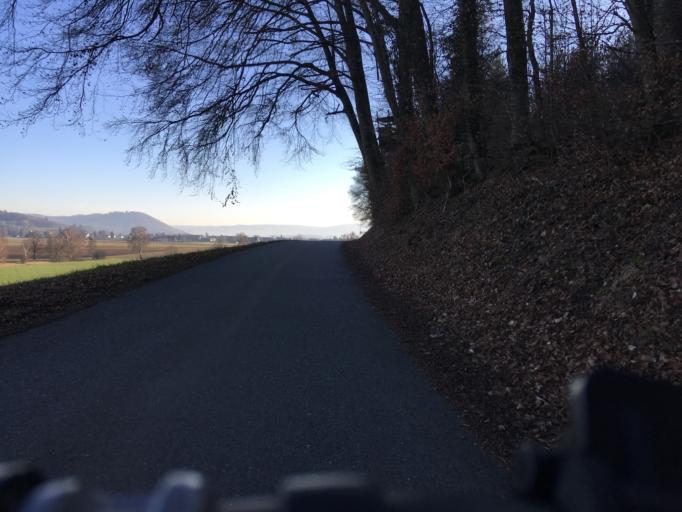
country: CH
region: Schaffhausen
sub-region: Bezirk Stein
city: Ramsen
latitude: 47.7194
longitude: 8.8084
